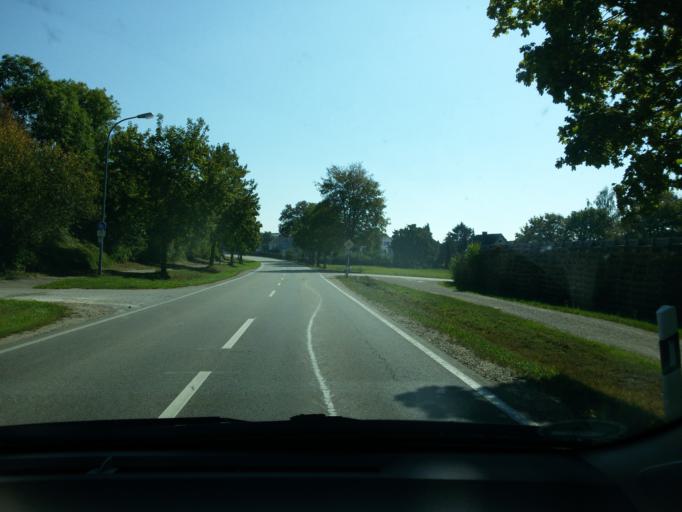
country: DE
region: Bavaria
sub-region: Swabia
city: Oettingen in Bayern
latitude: 48.9581
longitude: 10.5925
